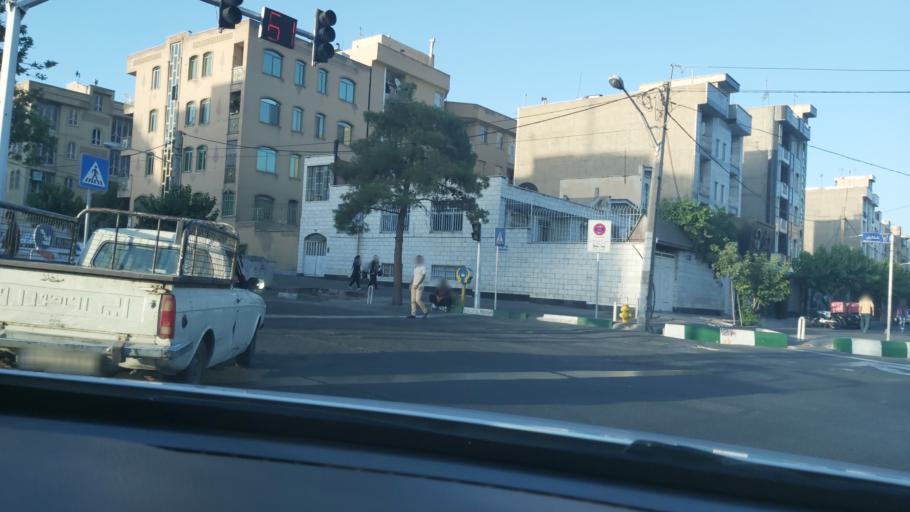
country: IR
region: Tehran
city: Tehran
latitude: 35.7273
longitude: 51.3041
